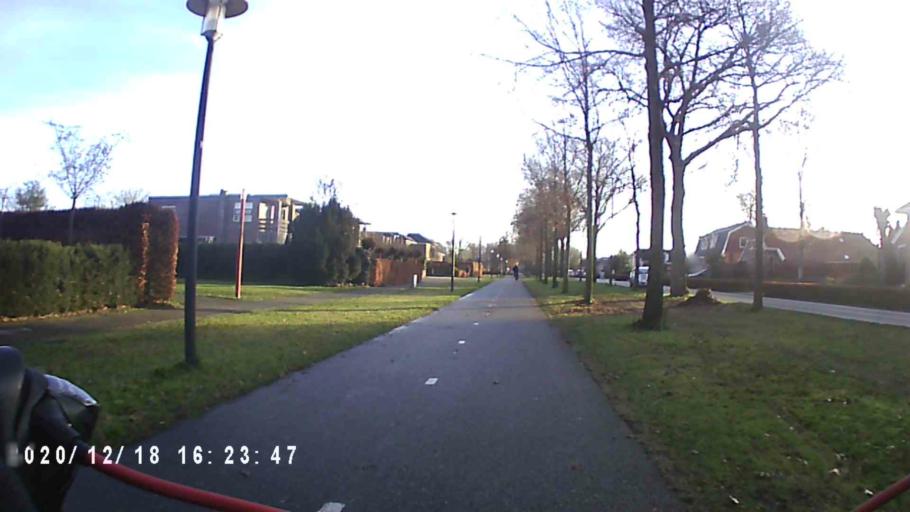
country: NL
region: Drenthe
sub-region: Gemeente Tynaarlo
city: Zuidlaren
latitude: 53.0885
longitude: 6.6928
